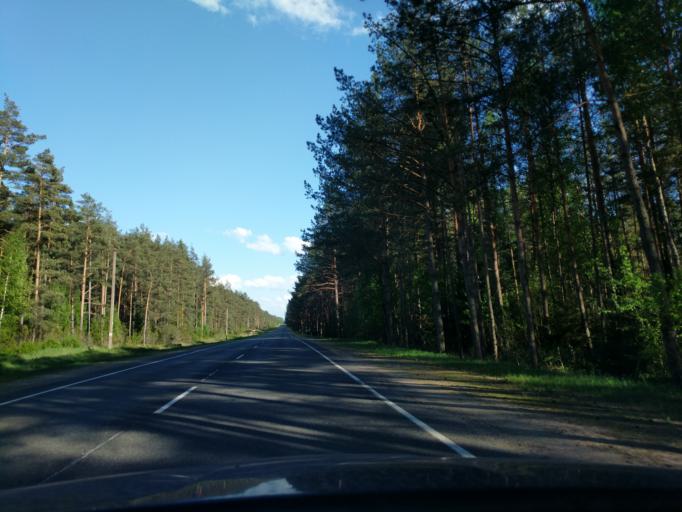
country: BY
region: Minsk
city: Myadzyel
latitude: 54.8251
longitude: 26.9484
